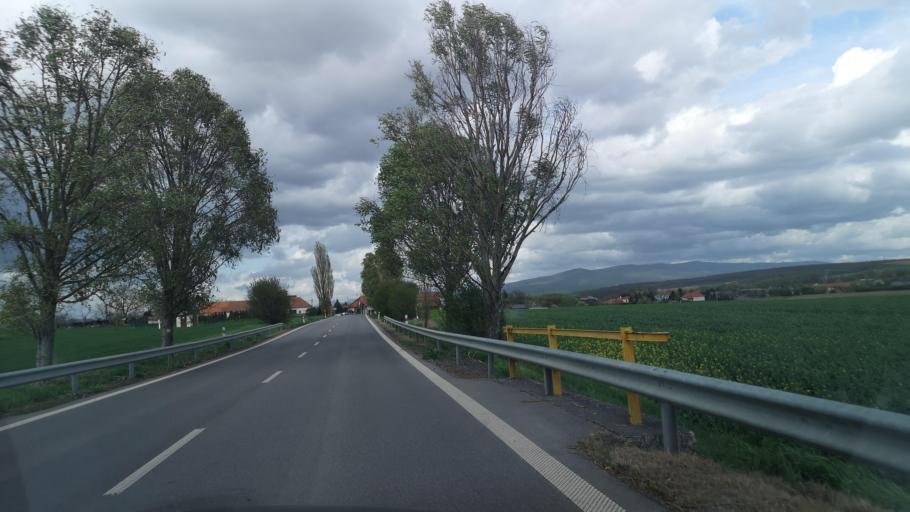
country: SK
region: Nitriansky
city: Zlate Moravce
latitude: 48.3254
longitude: 18.3481
